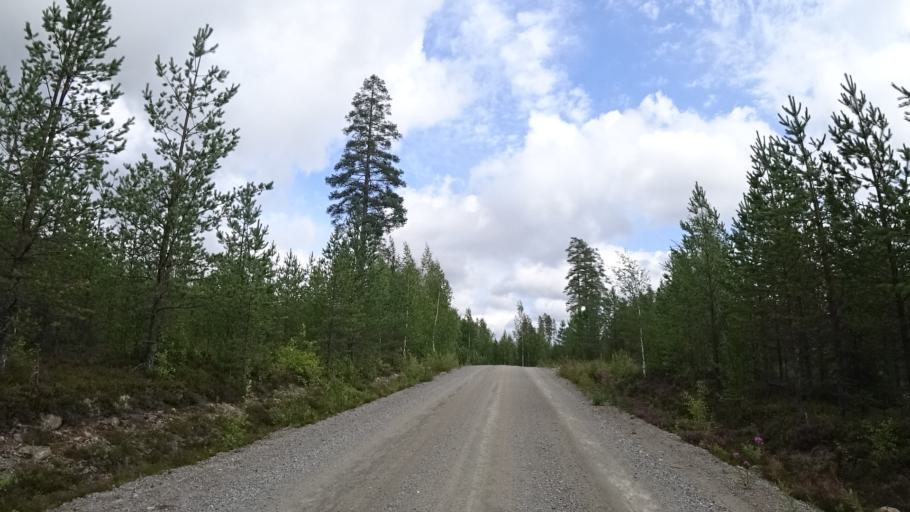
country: FI
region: North Karelia
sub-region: Joensuu
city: Ilomantsi
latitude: 62.9273
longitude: 31.3679
